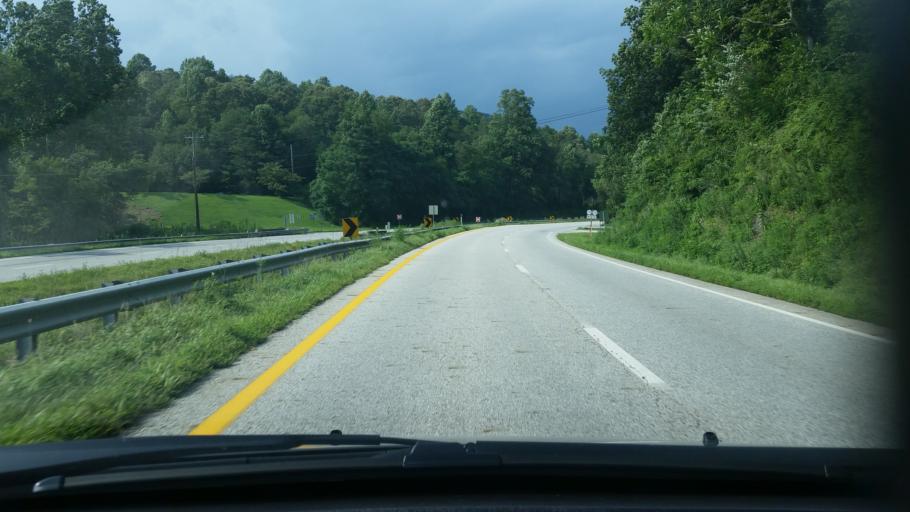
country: US
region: Virginia
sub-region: Nelson County
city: Lovingston
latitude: 37.8039
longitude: -78.8621
